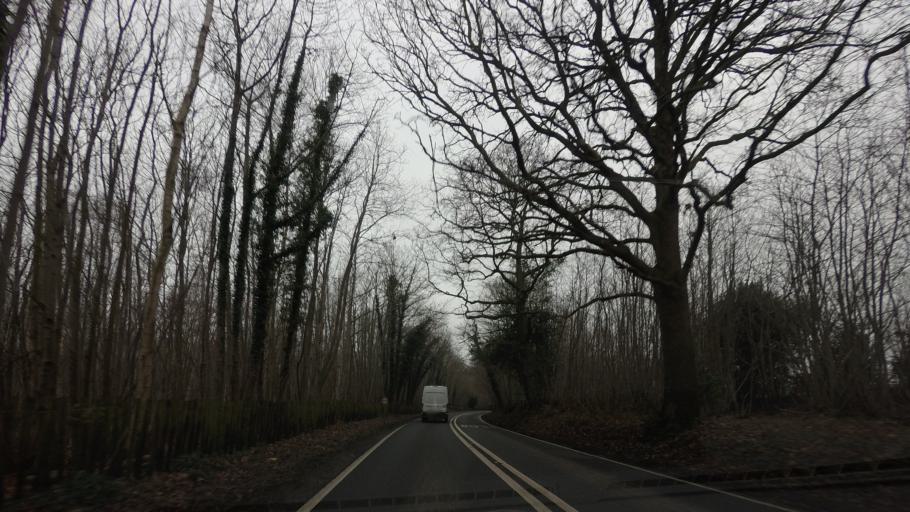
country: GB
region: England
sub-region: Kent
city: Staplehurst
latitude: 51.1268
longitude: 0.5615
